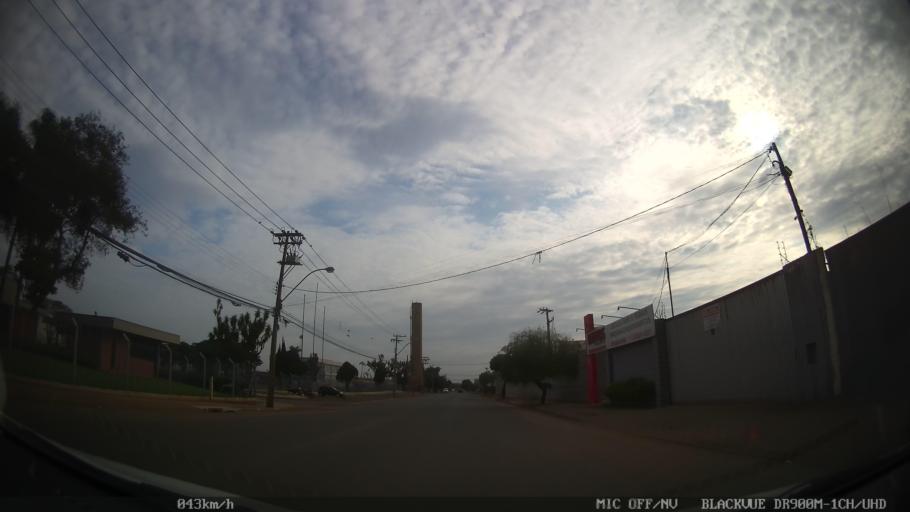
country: BR
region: Sao Paulo
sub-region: Santa Barbara D'Oeste
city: Santa Barbara d'Oeste
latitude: -22.7572
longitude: -47.3863
